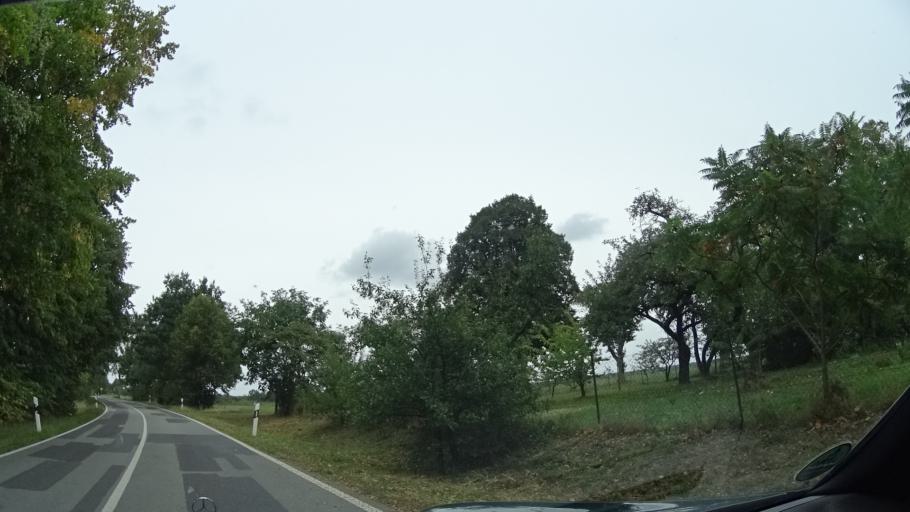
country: DE
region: Brandenburg
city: Walsleben
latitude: 52.9566
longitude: 12.7075
